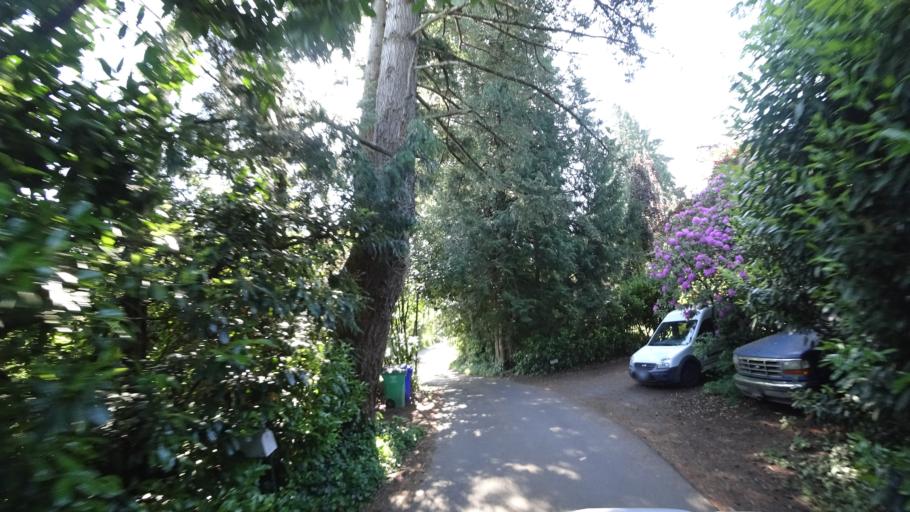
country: US
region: Oregon
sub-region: Clackamas County
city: Happy Valley
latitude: 45.4720
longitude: -122.5320
